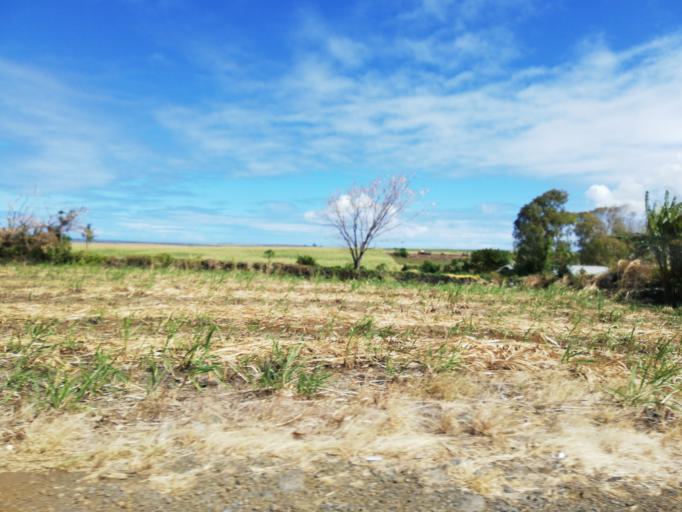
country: MU
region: Grand Port
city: Plaine Magnien
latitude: -20.4489
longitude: 57.6655
